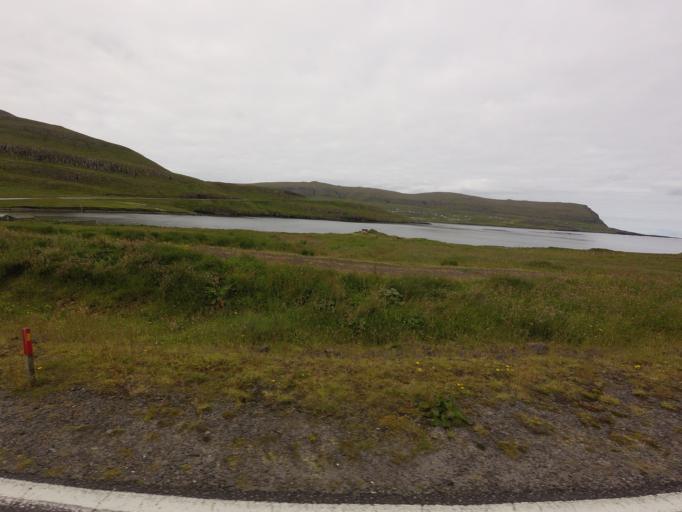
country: FO
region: Suduroy
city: Tvoroyri
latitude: 61.5321
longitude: -6.8078
